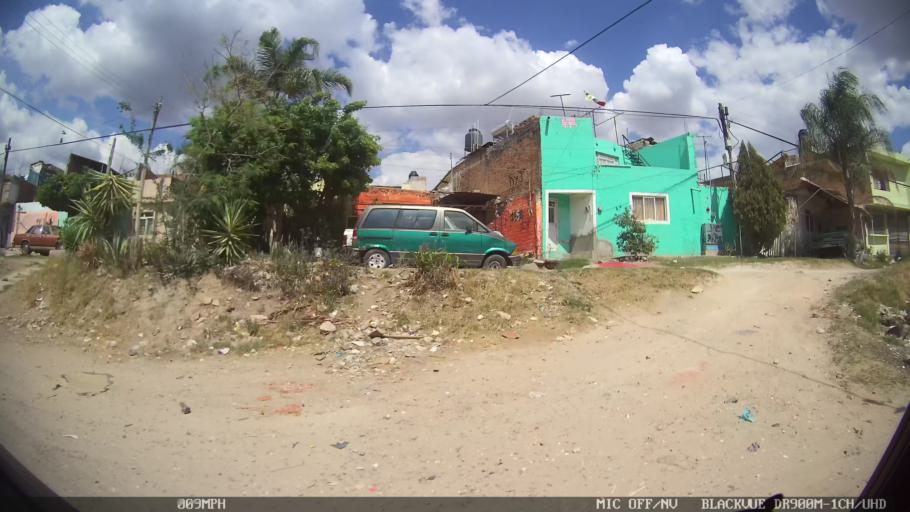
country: MX
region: Jalisco
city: Tlaquepaque
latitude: 20.6869
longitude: -103.2670
